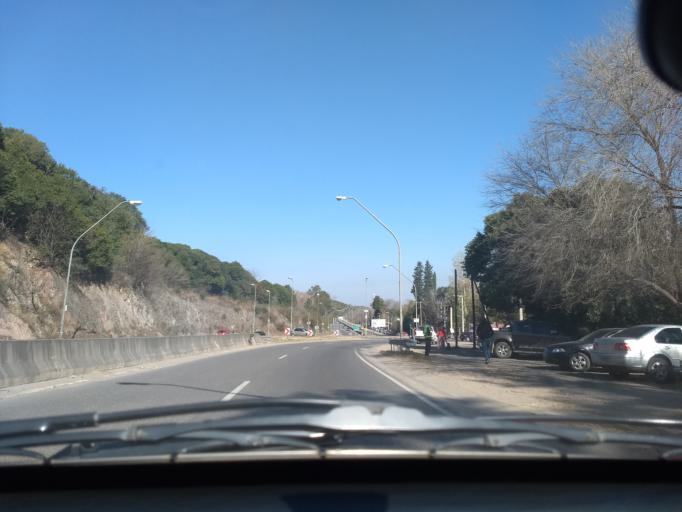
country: AR
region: Cordoba
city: Rio Ceballos
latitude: -31.1597
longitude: -64.3010
